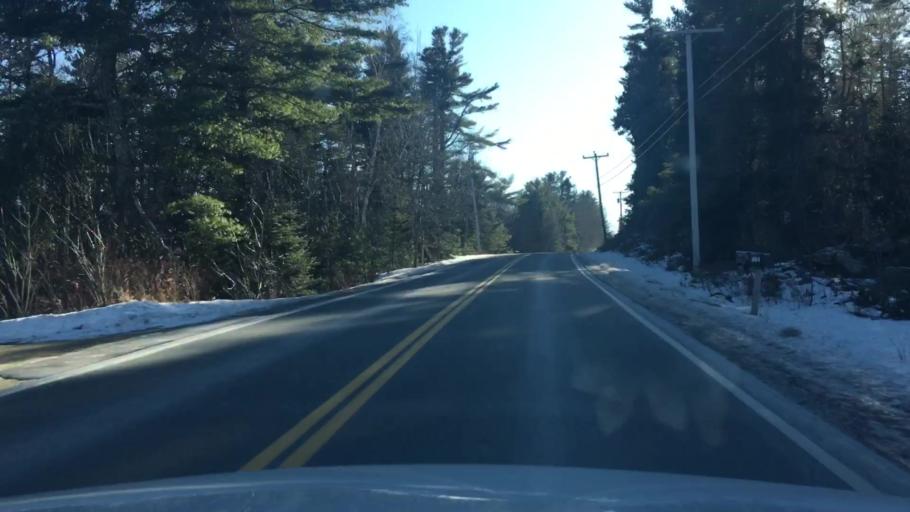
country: US
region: Maine
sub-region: Hancock County
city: Orland
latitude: 44.5180
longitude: -68.7504
